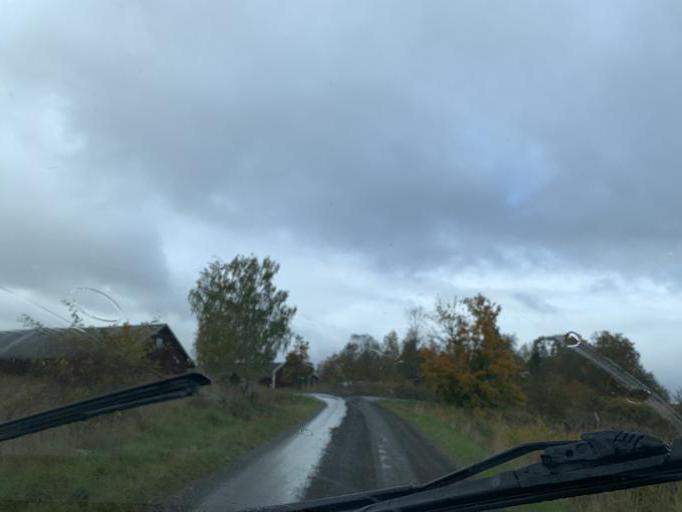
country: SE
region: Soedermanland
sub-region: Eskilstuna Kommun
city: Kvicksund
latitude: 59.3412
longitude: 16.2984
